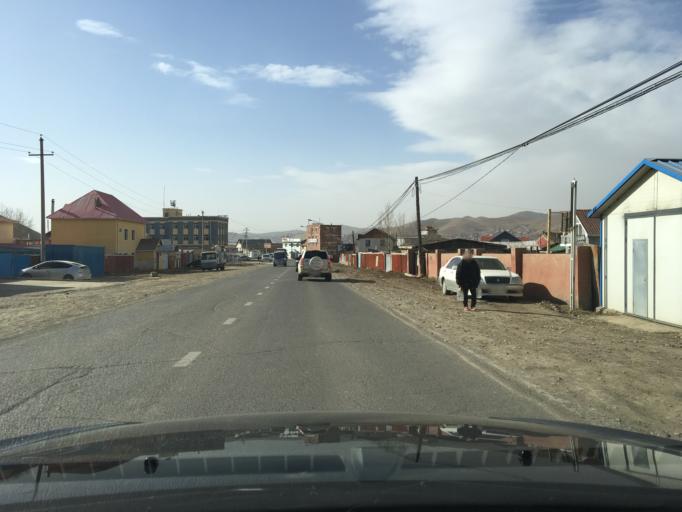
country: MN
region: Ulaanbaatar
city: Ulaanbaatar
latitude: 47.9834
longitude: 106.9415
